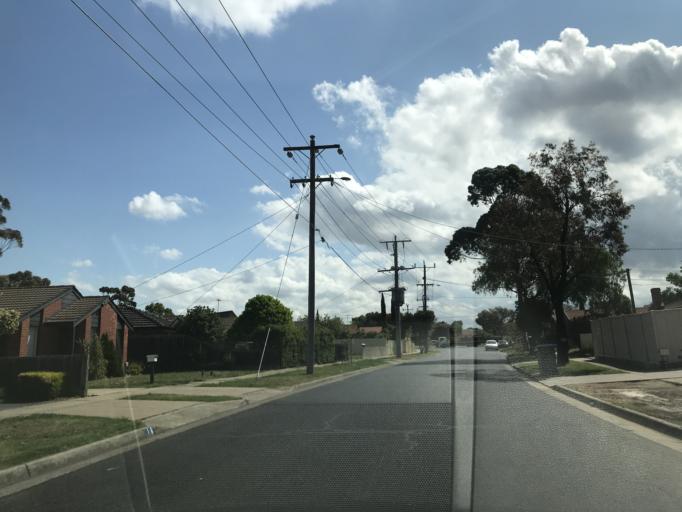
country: AU
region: Victoria
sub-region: Wyndham
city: Hoppers Crossing
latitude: -37.8689
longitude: 144.7049
